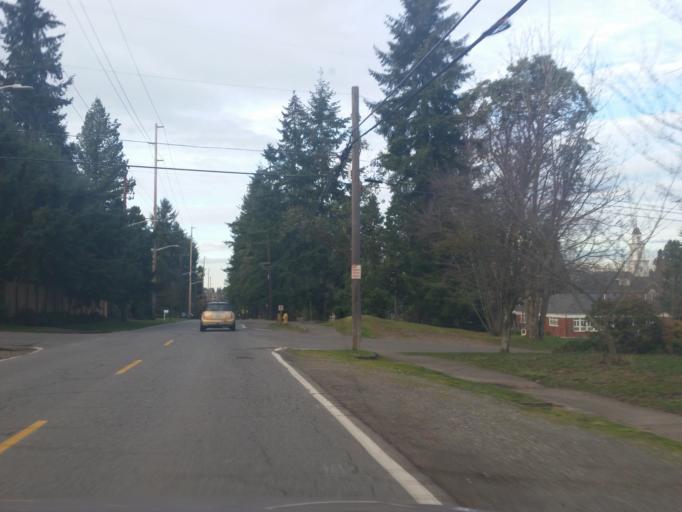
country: US
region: Washington
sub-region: King County
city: Shoreline
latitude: 47.7301
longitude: -122.3289
